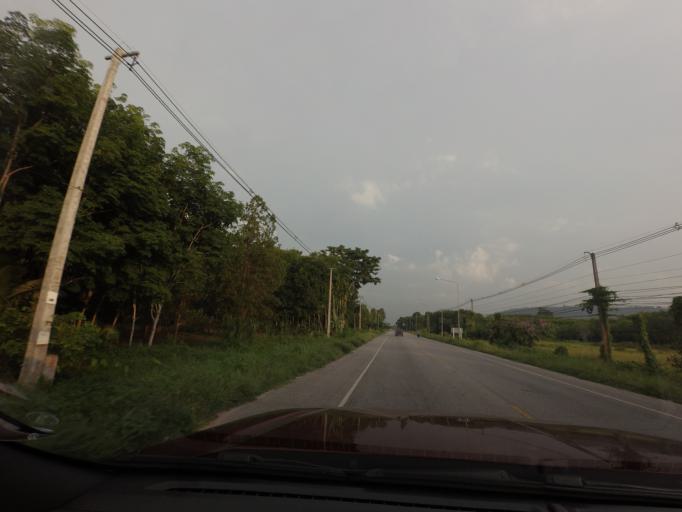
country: TH
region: Pattani
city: Mae Lan
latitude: 6.6306
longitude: 101.1871
